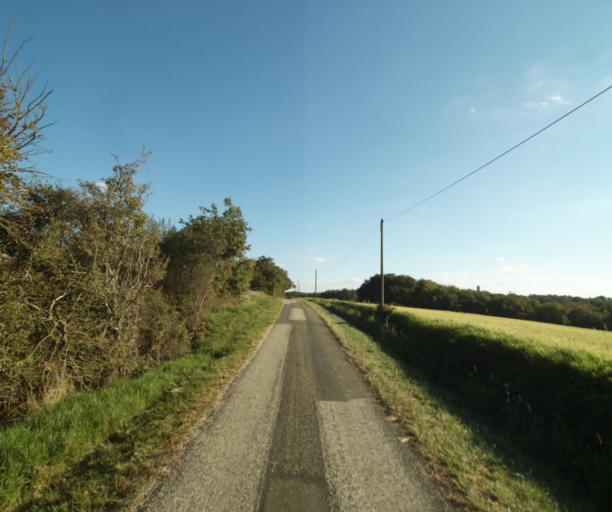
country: FR
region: Midi-Pyrenees
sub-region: Departement du Gers
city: Eauze
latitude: 43.7873
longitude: 0.1210
